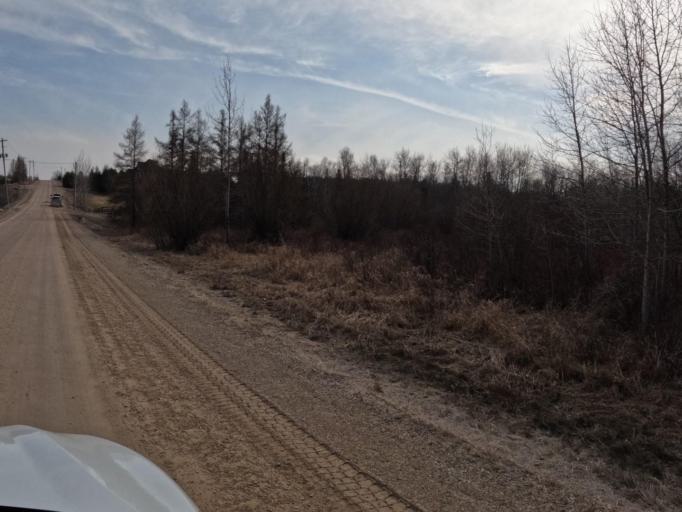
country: CA
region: Ontario
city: Orangeville
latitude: 43.8908
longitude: -80.2992
